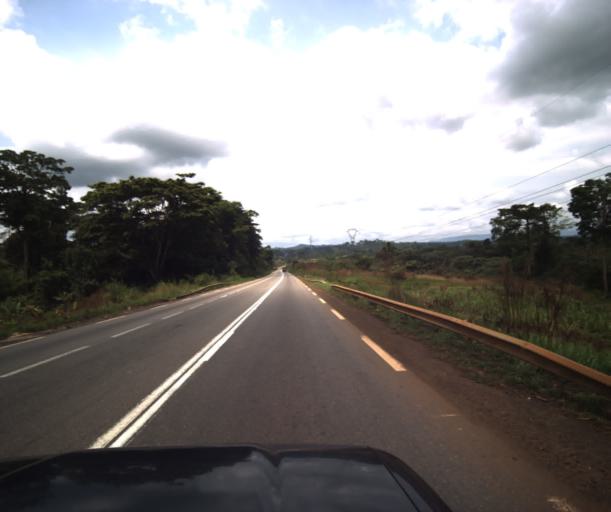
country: CM
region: Centre
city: Eseka
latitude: 3.8530
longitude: 10.9566
